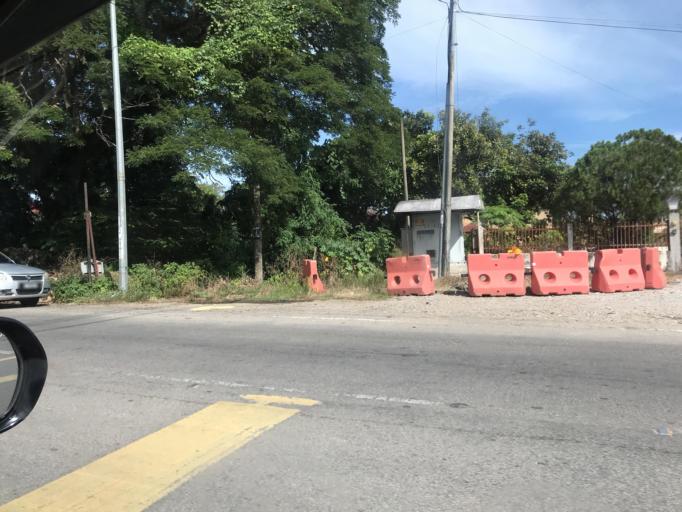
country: MY
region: Kelantan
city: Kota Bharu
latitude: 6.1198
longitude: 102.1973
